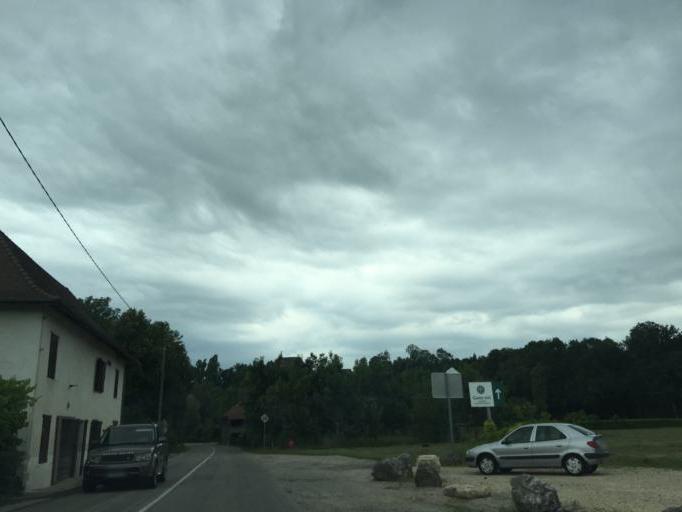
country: FR
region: Rhone-Alpes
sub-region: Departement de la Savoie
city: Le Pont-de-Beauvoisin
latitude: 45.5566
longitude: 5.6759
